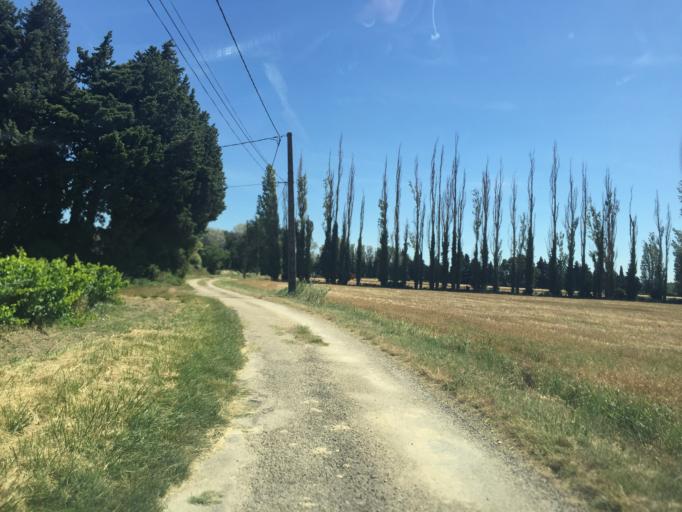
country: FR
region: Provence-Alpes-Cote d'Azur
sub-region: Departement du Vaucluse
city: Courthezon
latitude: 44.0767
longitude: 4.9019
